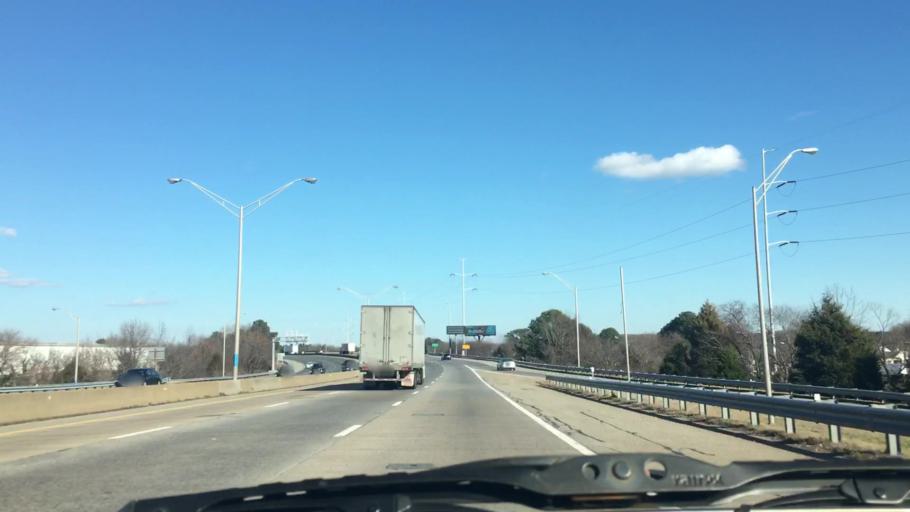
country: US
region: Virginia
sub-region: City of Newport News
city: Newport News
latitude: 36.9958
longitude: -76.4076
